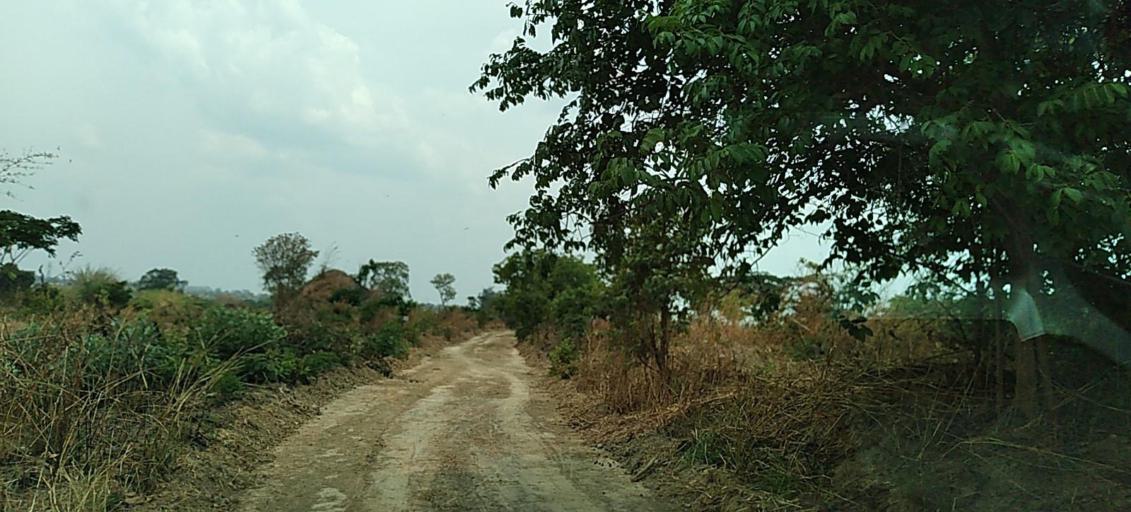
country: ZM
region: Copperbelt
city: Chililabombwe
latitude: -12.3555
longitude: 27.7990
